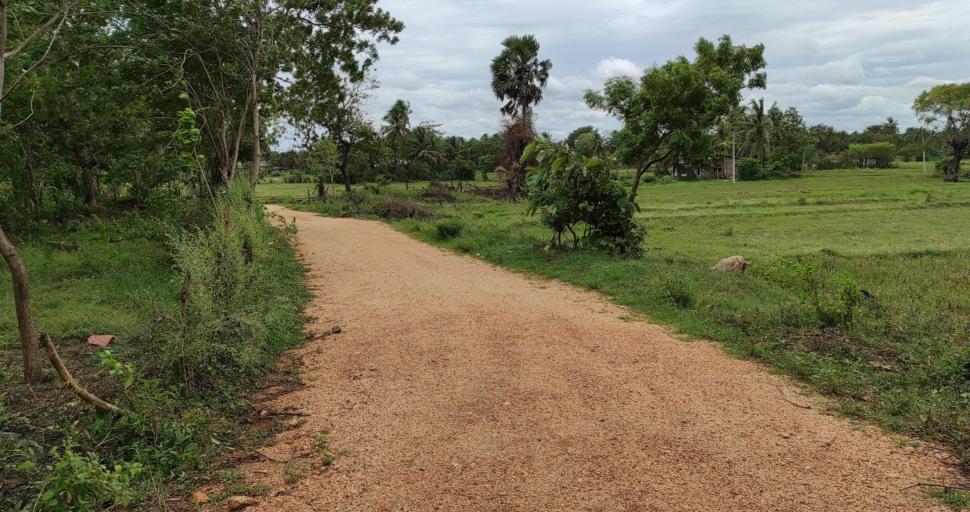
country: LK
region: Eastern Province
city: Trincomalee
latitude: 8.4463
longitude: 81.0510
